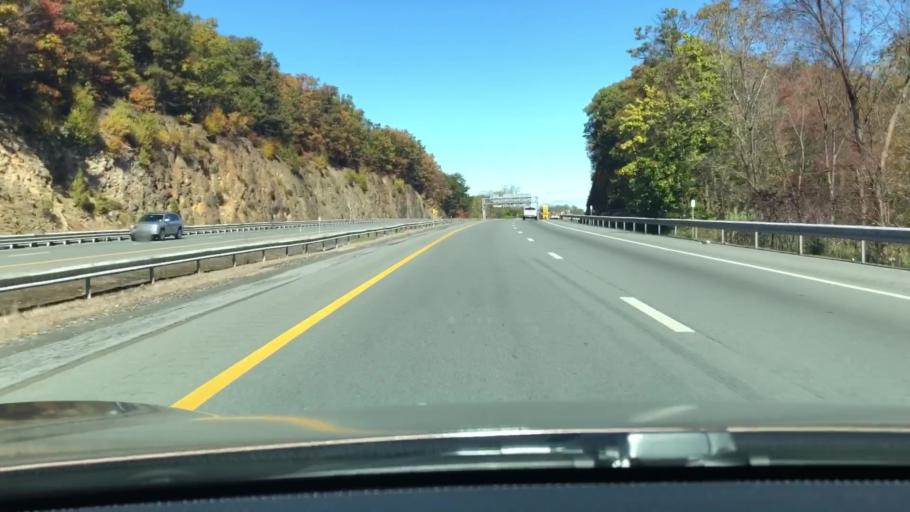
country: US
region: New York
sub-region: Orange County
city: Highland Mills
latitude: 41.3460
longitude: -74.1165
